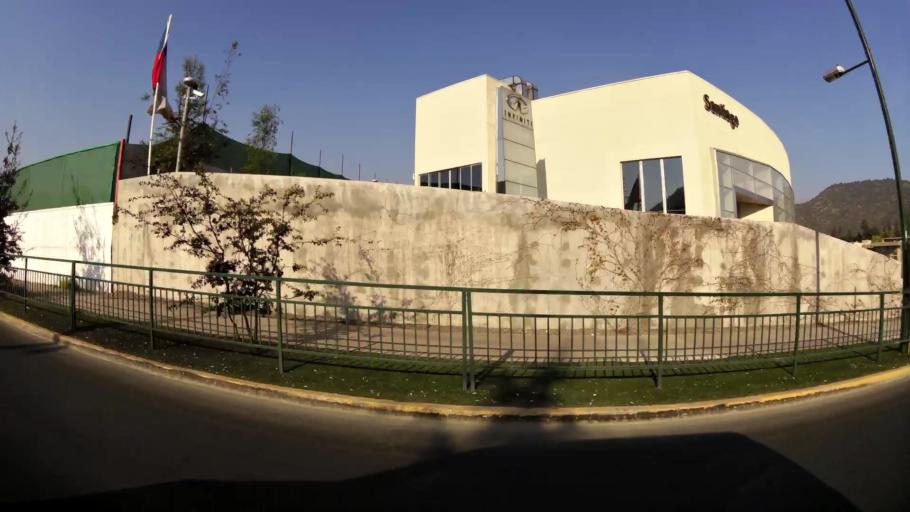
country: CL
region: Santiago Metropolitan
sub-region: Provincia de Santiago
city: Villa Presidente Frei, Nunoa, Santiago, Chile
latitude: -33.3609
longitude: -70.5441
